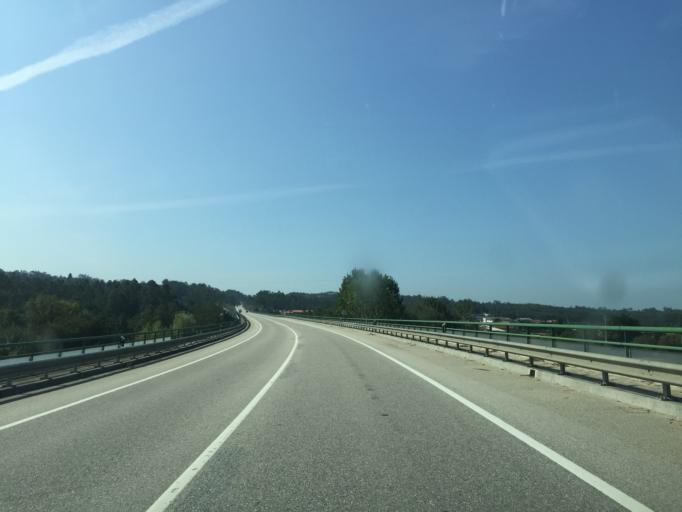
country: PT
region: Leiria
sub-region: Pombal
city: Lourical
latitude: 39.9792
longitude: -8.7031
